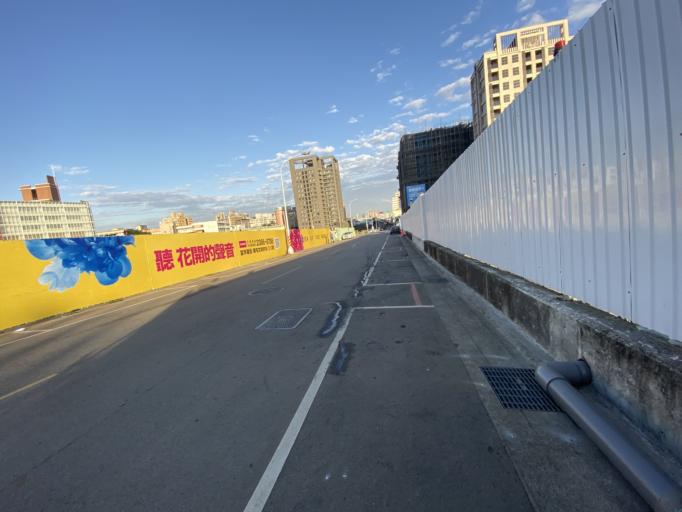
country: TW
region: Taiwan
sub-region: Taichung City
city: Taichung
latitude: 24.1357
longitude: 120.6080
